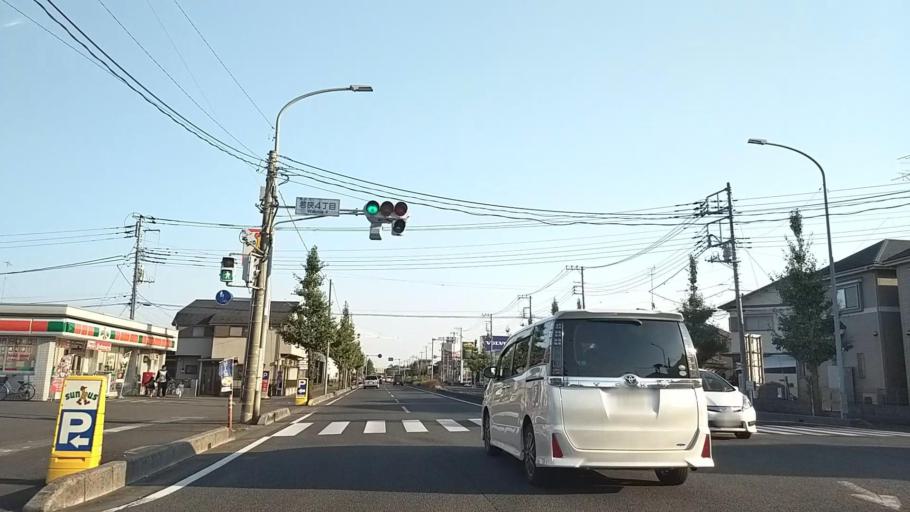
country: JP
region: Saitama
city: Sayama
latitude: 35.8024
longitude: 139.4148
